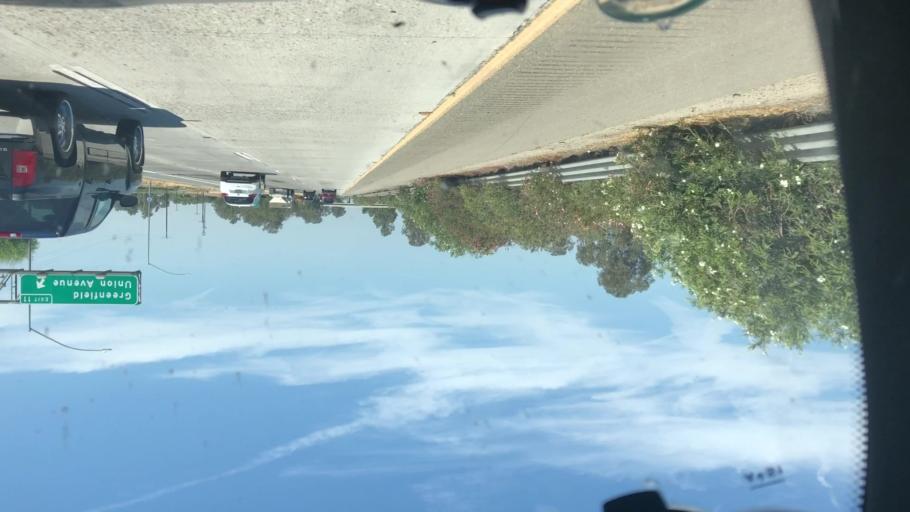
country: US
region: California
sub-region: Kern County
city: Greenfield
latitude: 35.1675
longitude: -119.0025
